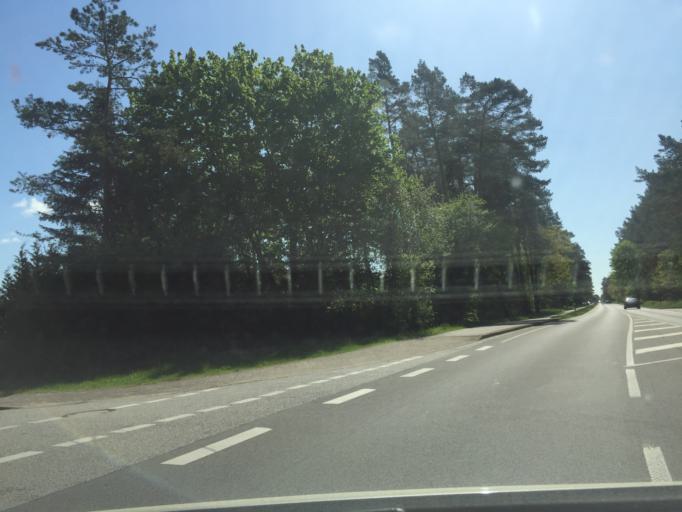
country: DE
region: Mecklenburg-Vorpommern
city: Torgelow
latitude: 53.6166
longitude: 14.0323
